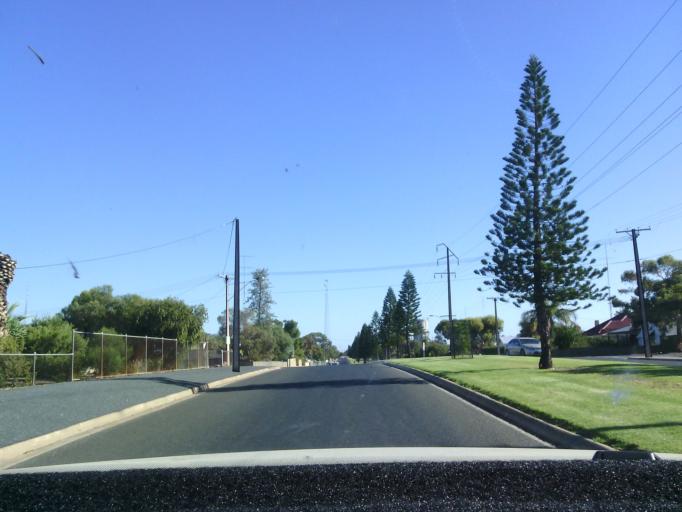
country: AU
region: South Australia
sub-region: Berri and Barmera
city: Berri
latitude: -34.2782
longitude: 140.5972
